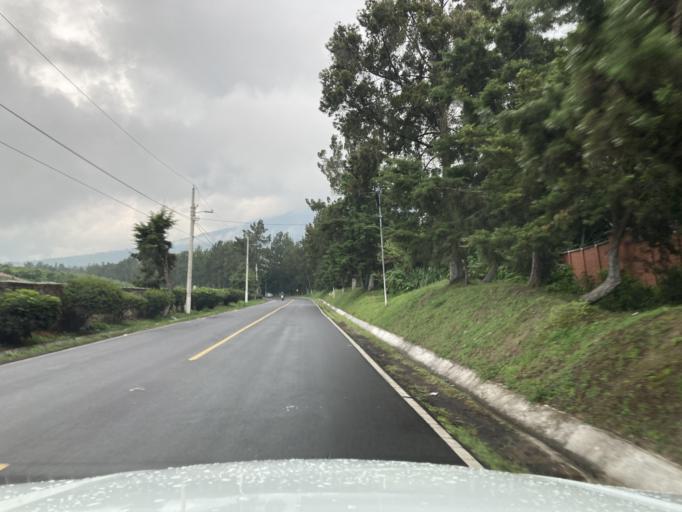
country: GT
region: Sacatepequez
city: San Miguel Duenas
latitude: 14.5194
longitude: -90.7891
